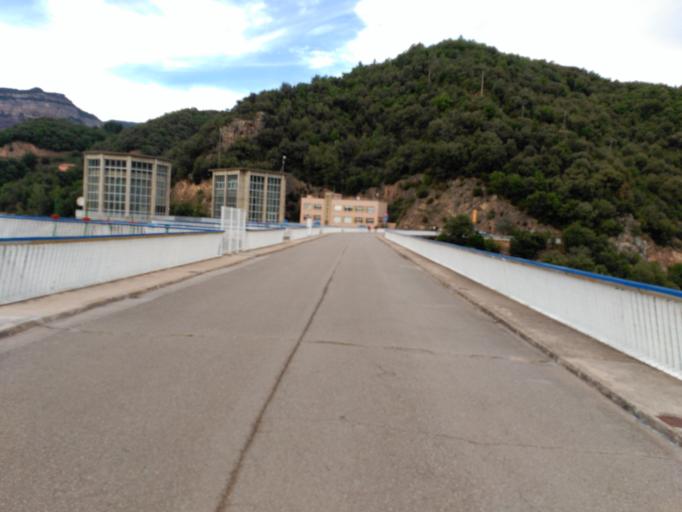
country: ES
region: Catalonia
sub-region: Provincia de Barcelona
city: Tavertet
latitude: 41.9676
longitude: 2.4124
